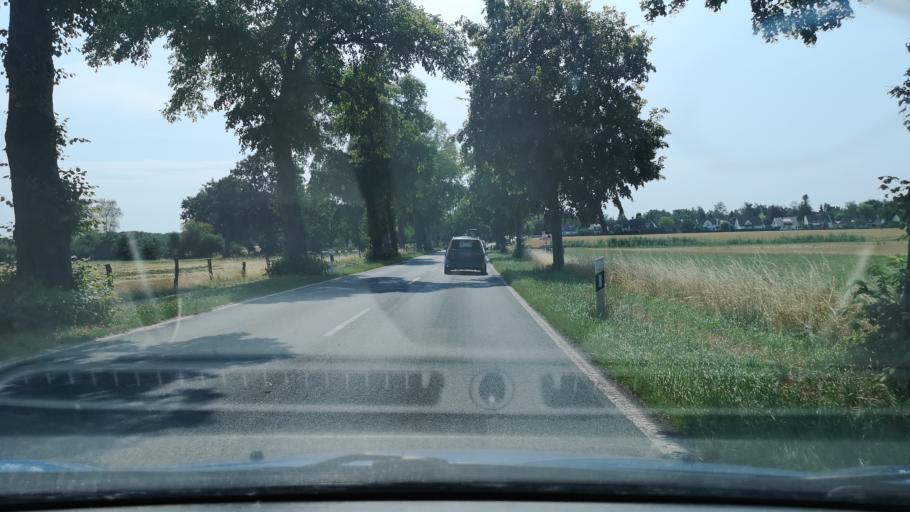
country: DE
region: Lower Saxony
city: Isernhagen Farster Bauerschaft
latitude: 52.4519
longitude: 9.7994
